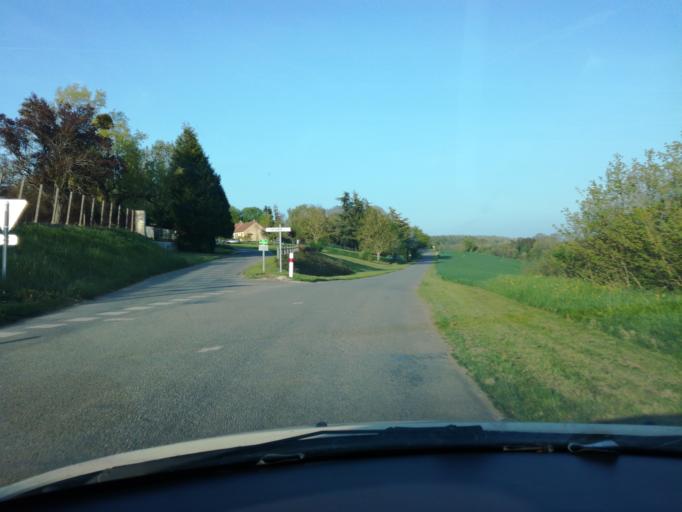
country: FR
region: Picardie
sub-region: Departement de la Somme
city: Poix-de-Picardie
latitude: 49.8167
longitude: 1.9949
